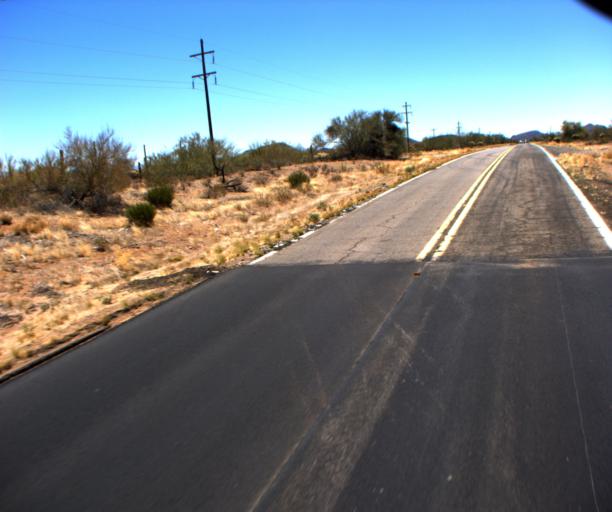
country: US
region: Arizona
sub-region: Pima County
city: Sells
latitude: 32.0149
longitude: -111.9972
